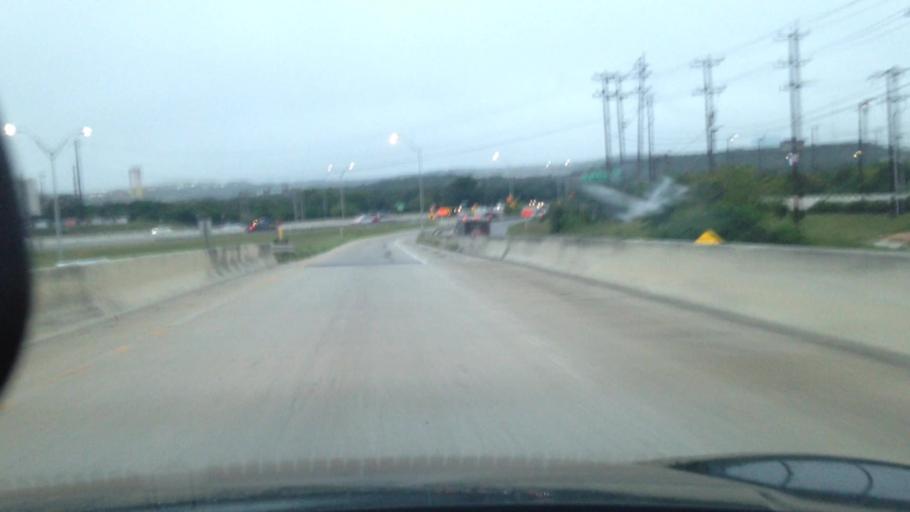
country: US
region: Texas
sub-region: Bexar County
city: Shavano Park
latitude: 29.5920
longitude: -98.5971
